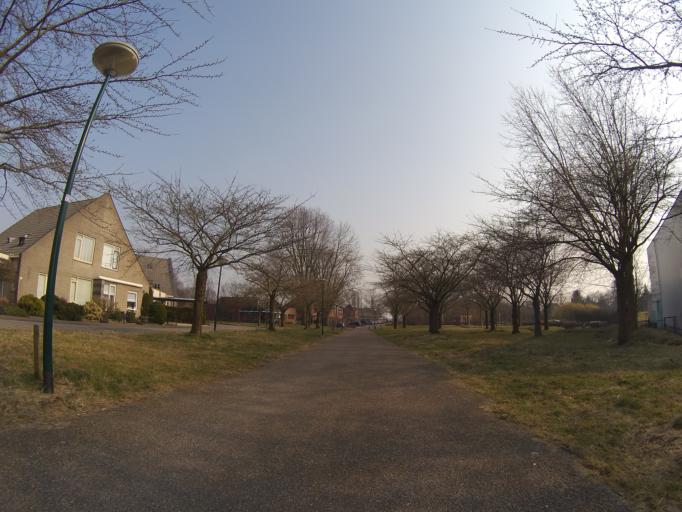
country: NL
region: Utrecht
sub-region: Gemeente Soest
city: Soest
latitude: 52.1770
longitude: 5.2974
